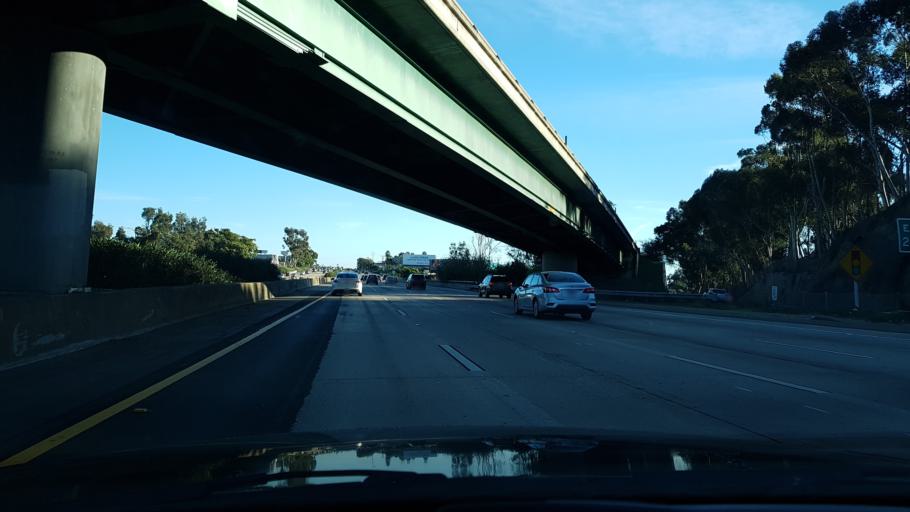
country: US
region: California
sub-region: San Diego County
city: La Jolla
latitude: 32.8121
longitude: -117.2203
